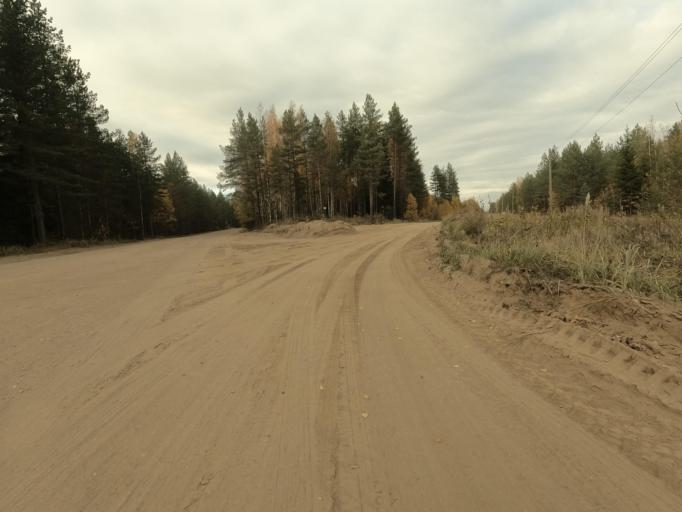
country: RU
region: Leningrad
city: Priladozhskiy
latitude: 59.6886
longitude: 31.3605
